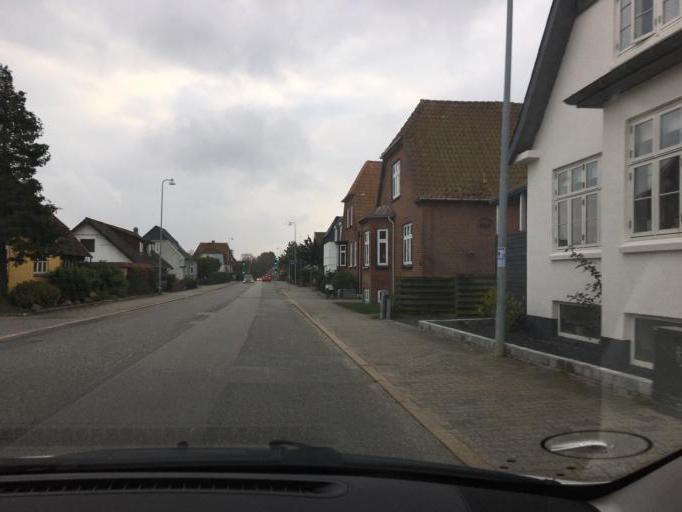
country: DK
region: South Denmark
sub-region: Fredericia Kommune
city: Fredericia
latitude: 55.5732
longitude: 9.7534
